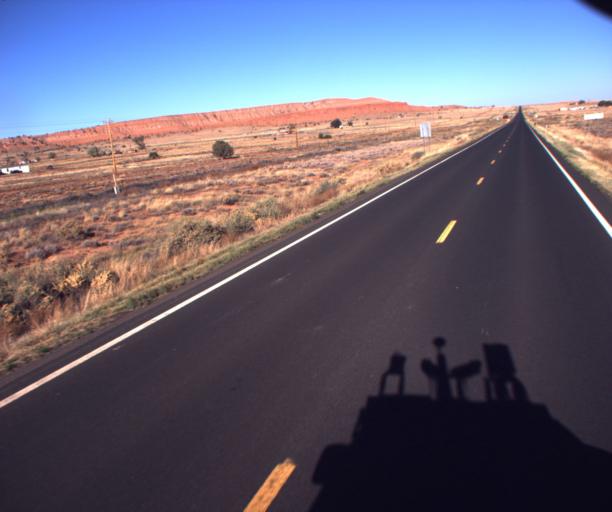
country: US
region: Arizona
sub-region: Apache County
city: Ganado
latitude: 35.7595
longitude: -109.6330
